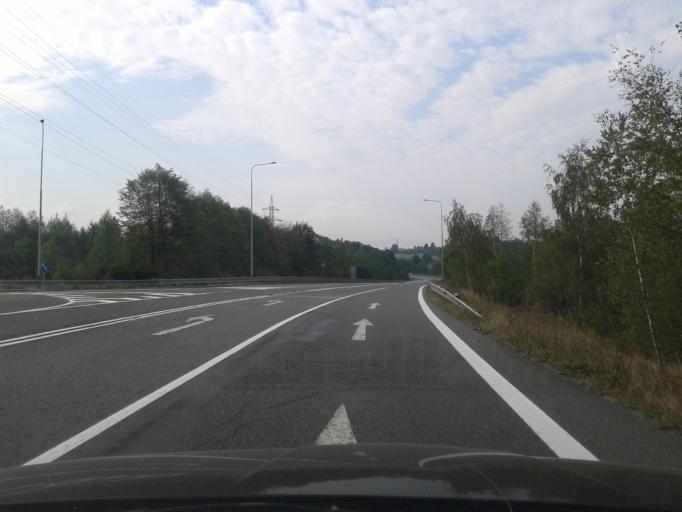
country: CZ
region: Moravskoslezsky
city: Orlova
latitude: 49.8144
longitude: 18.4363
